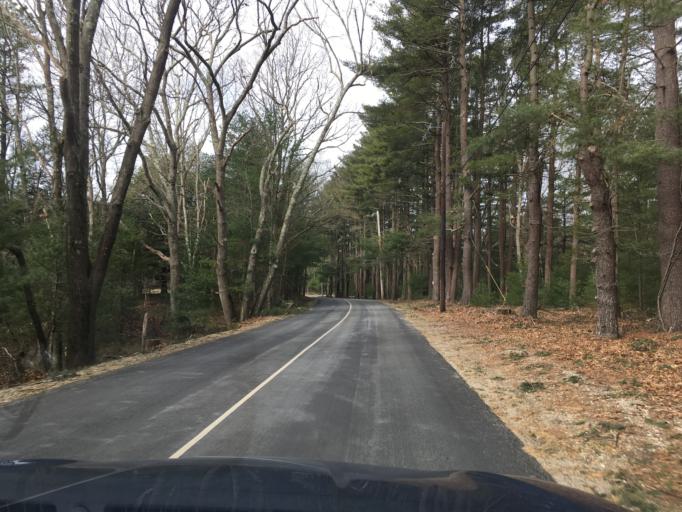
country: US
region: Rhode Island
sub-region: Kent County
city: East Greenwich
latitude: 41.6482
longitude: -71.4314
